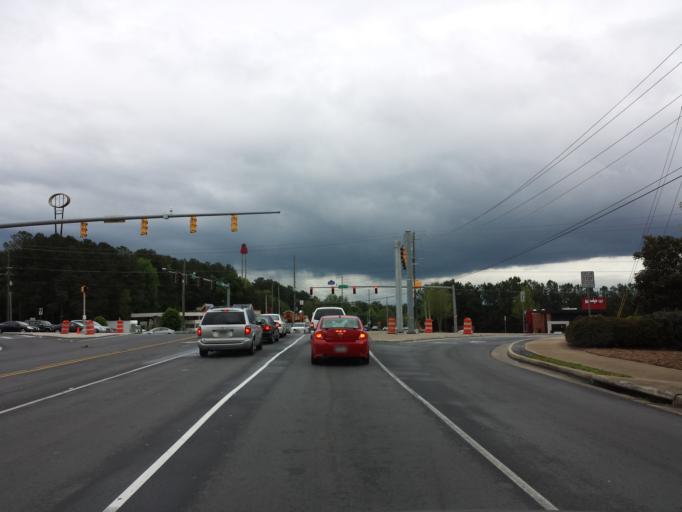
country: US
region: Georgia
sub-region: Cobb County
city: Kennesaw
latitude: 34.0333
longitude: -84.5801
